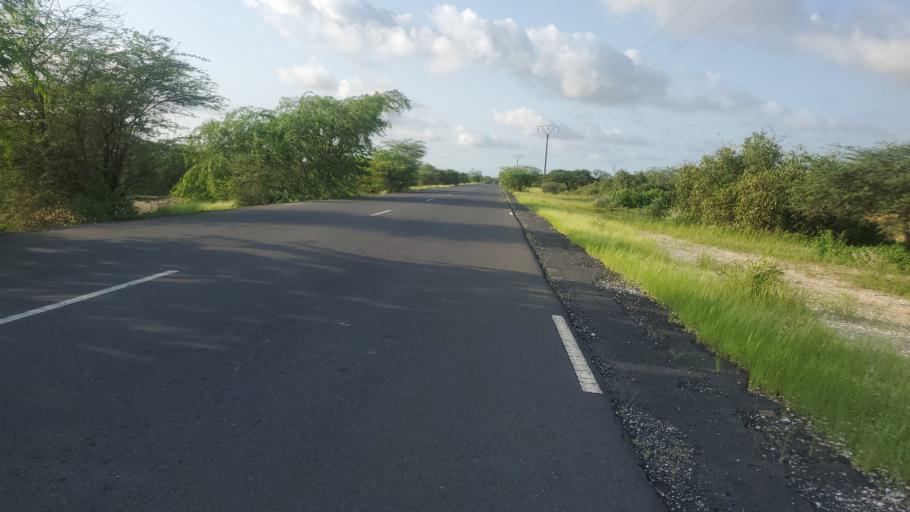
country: SN
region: Saint-Louis
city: Saint-Louis
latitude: 16.1145
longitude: -16.4135
